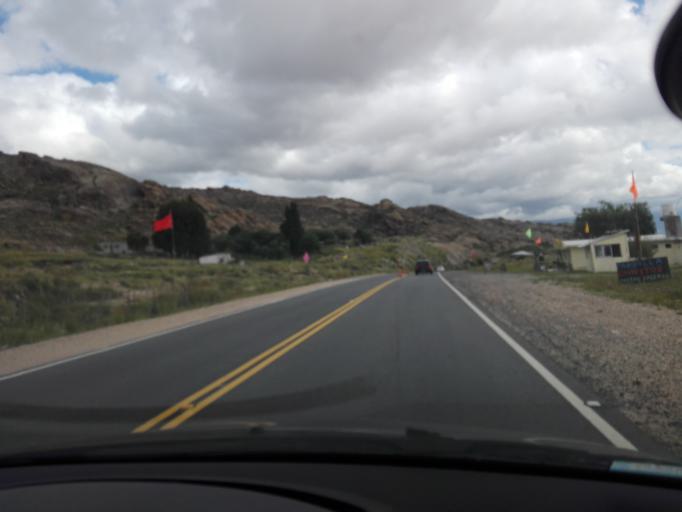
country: AR
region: Cordoba
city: Mina Clavero
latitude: -31.6964
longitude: -64.8950
